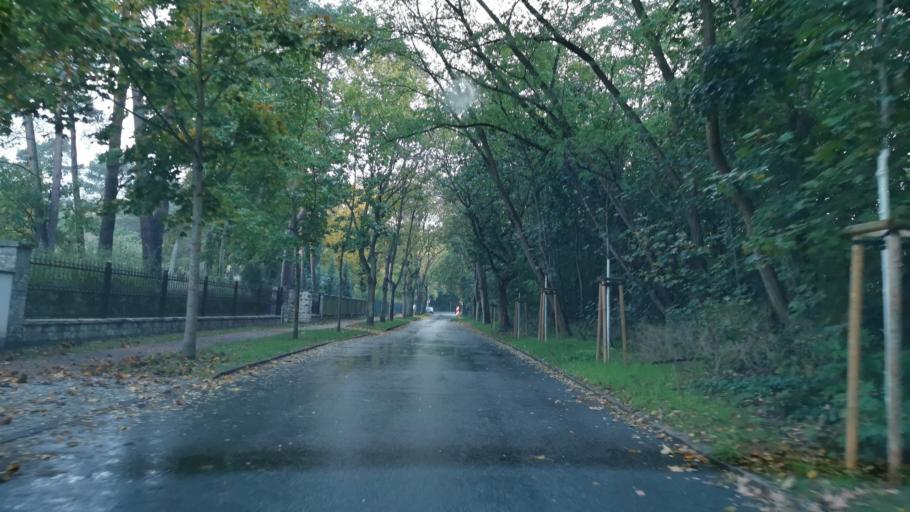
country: DE
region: Brandenburg
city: Michendorf
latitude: 52.3291
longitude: 13.0600
